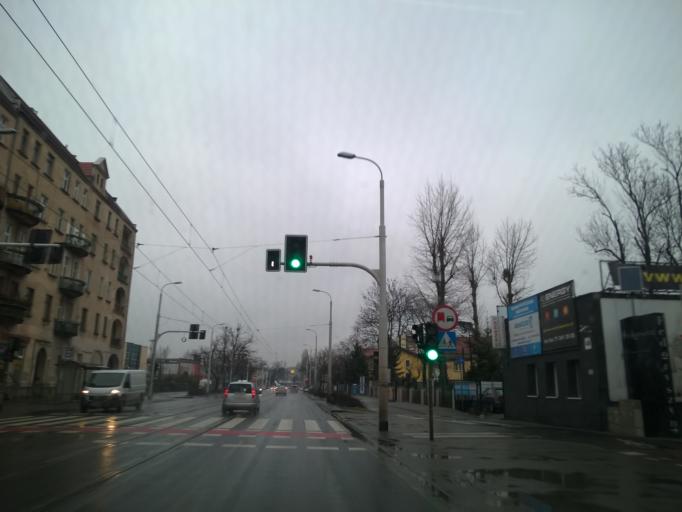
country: PL
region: Lower Silesian Voivodeship
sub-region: Powiat wroclawski
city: Wroclaw
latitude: 51.0933
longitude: 17.0603
